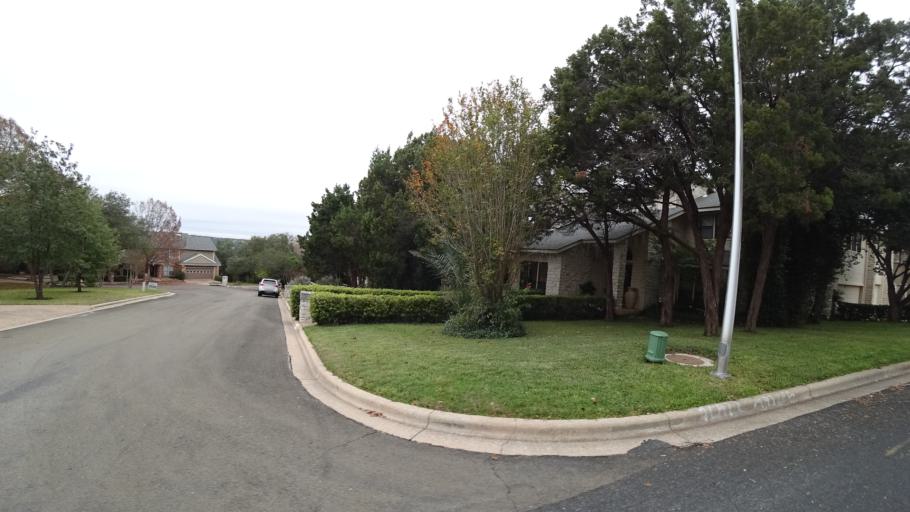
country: US
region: Texas
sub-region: Williamson County
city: Jollyville
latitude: 30.3748
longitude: -97.7957
